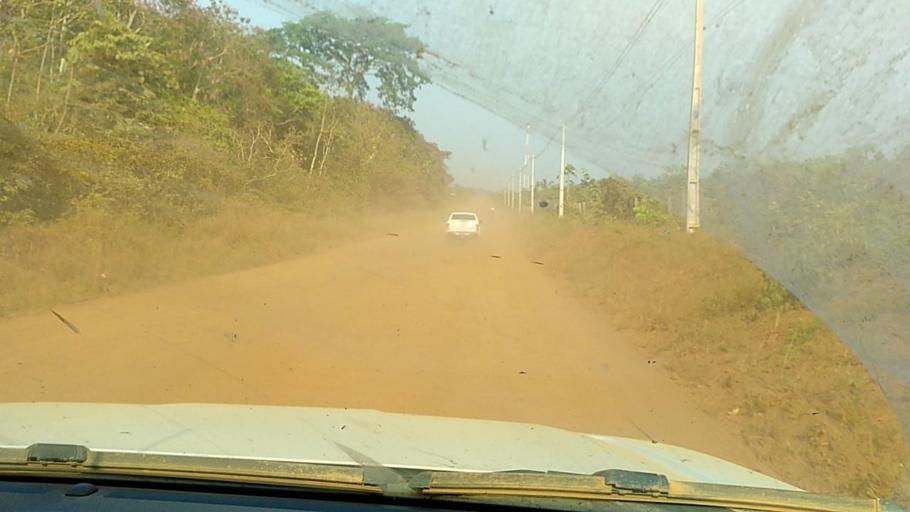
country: BR
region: Rondonia
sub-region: Porto Velho
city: Porto Velho
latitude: -8.7606
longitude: -63.9659
